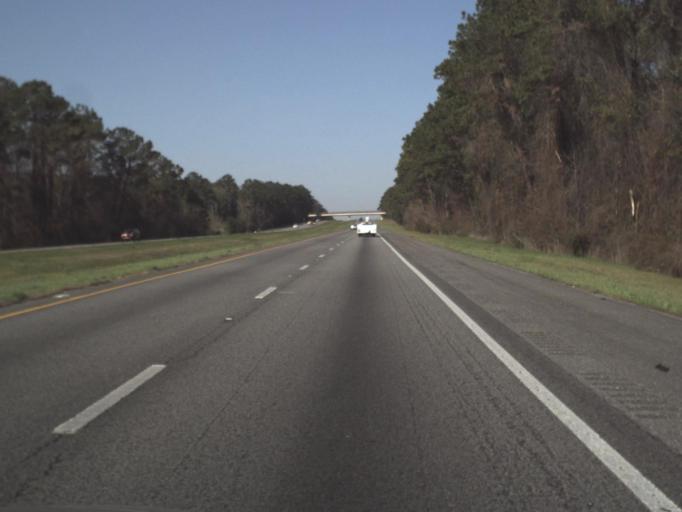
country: US
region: Florida
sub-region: Jefferson County
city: Monticello
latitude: 30.4886
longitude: -83.9742
